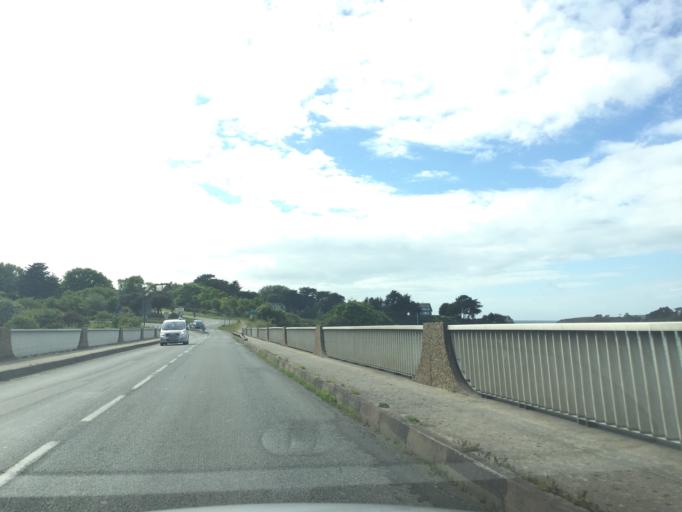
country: FR
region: Brittany
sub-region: Departement d'Ille-et-Vilaine
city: Saint-Briac-sur-Mer
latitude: 48.6165
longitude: -2.1401
